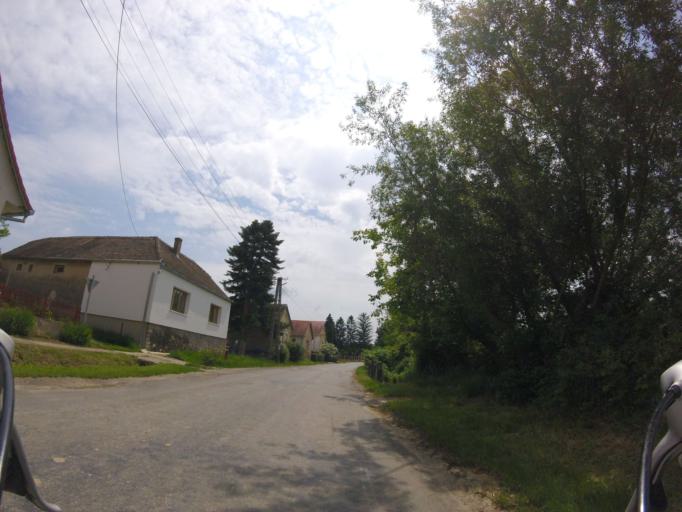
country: HU
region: Baranya
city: Kozarmisleny
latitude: 46.0203
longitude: 18.4068
